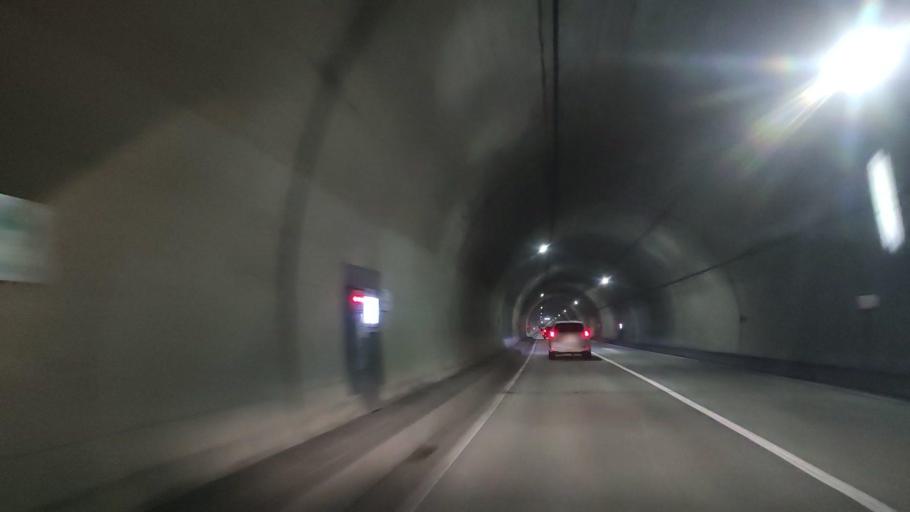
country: JP
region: Hokkaido
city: Ishikari
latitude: 43.5383
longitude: 141.3928
